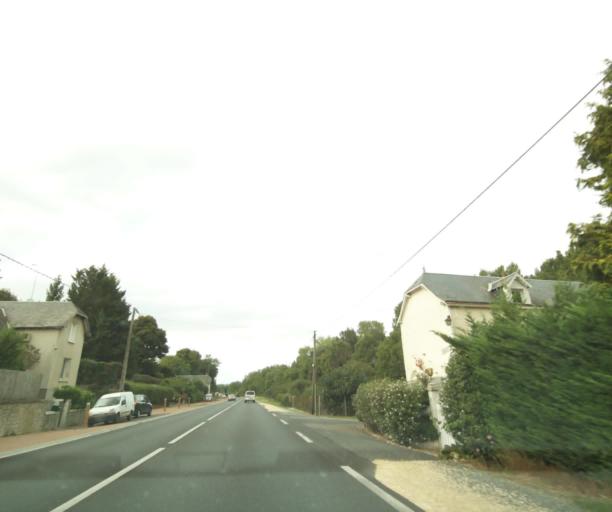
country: FR
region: Centre
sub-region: Departement d'Indre-et-Loire
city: Loches
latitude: 47.1502
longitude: 0.9994
